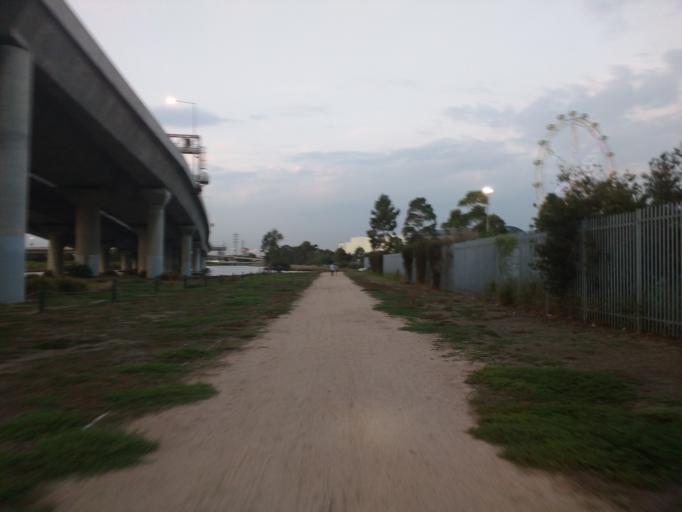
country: AU
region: Victoria
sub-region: Melbourne
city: Docklands
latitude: -37.8150
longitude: 144.9341
